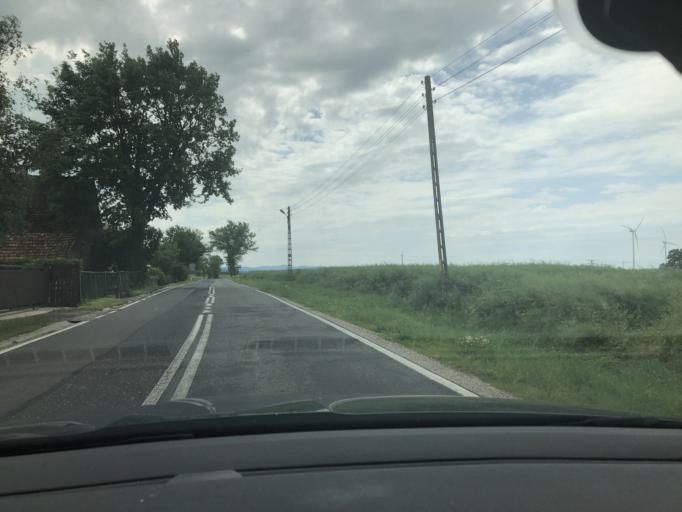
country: PL
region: Lower Silesian Voivodeship
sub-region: Powiat zlotoryjski
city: Zagrodno
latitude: 51.1873
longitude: 15.9264
